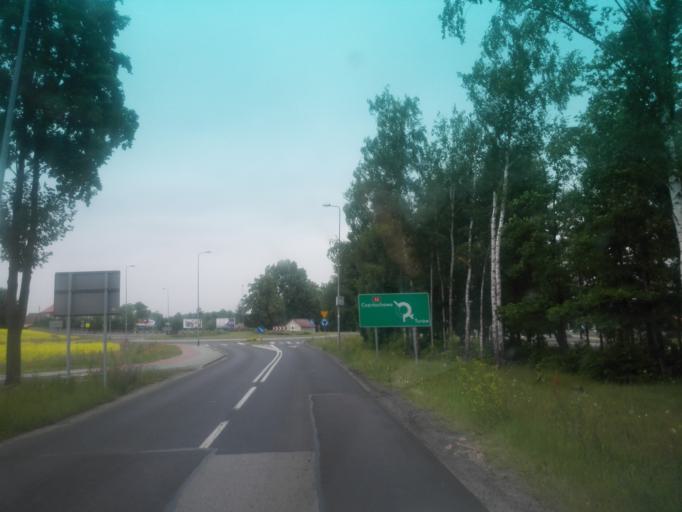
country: PL
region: Silesian Voivodeship
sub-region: Powiat czestochowski
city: Olsztyn
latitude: 50.7529
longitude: 19.2743
